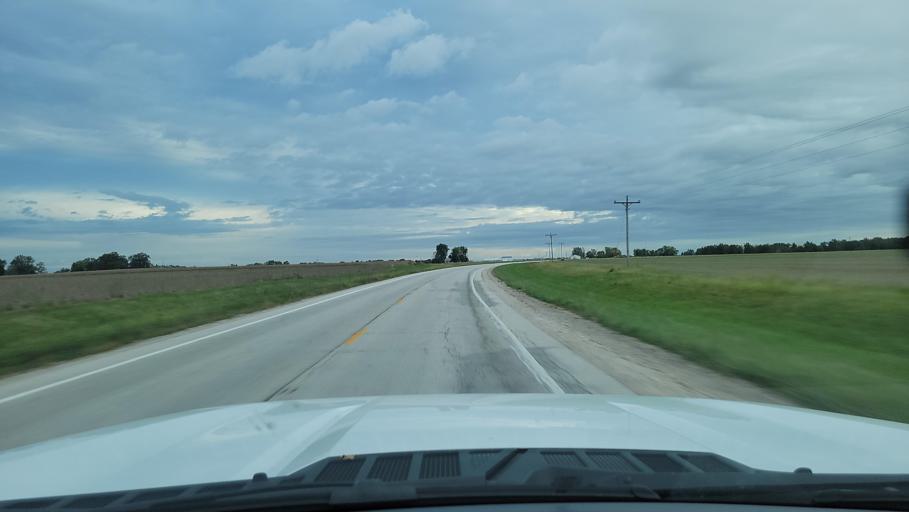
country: US
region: Illinois
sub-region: Schuyler County
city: Rushville
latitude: 40.0751
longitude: -90.6150
